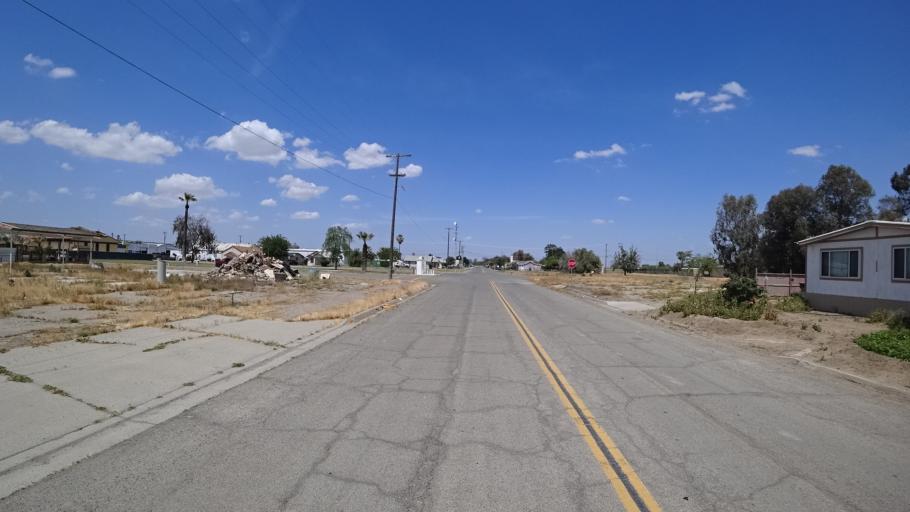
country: US
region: California
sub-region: Kings County
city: Stratford
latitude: 36.1889
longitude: -119.8206
